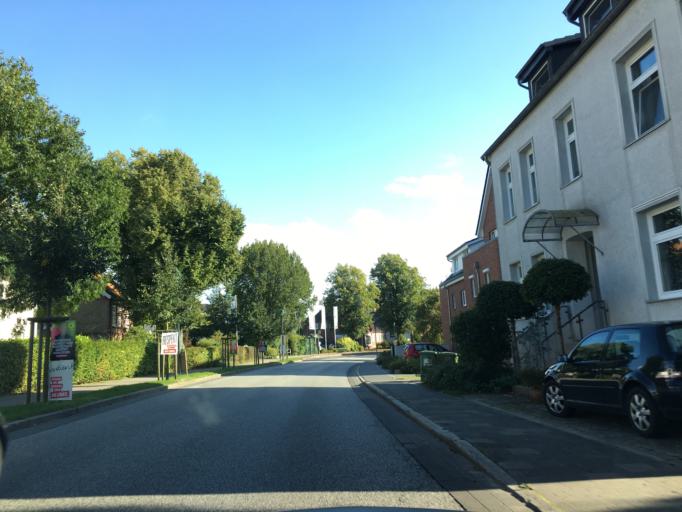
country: DE
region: Schleswig-Holstein
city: Heikendorf
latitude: 54.3684
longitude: 10.2029
